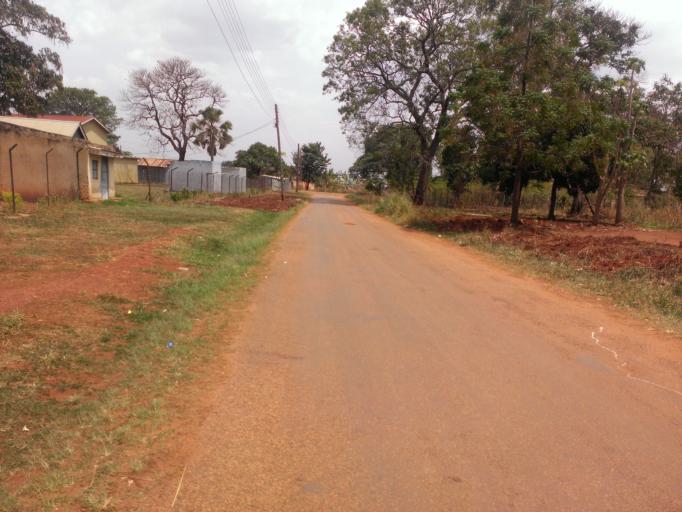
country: UG
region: Northern Region
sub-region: Gulu District
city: Gulu
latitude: 2.7850
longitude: 32.3062
